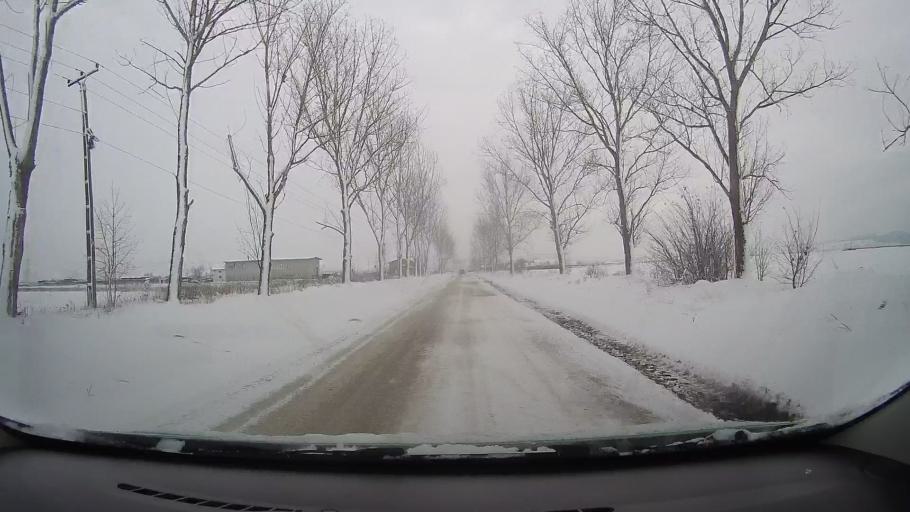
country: RO
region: Alba
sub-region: Municipiul Sebes
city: Lancram
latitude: 45.9603
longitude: 23.5262
